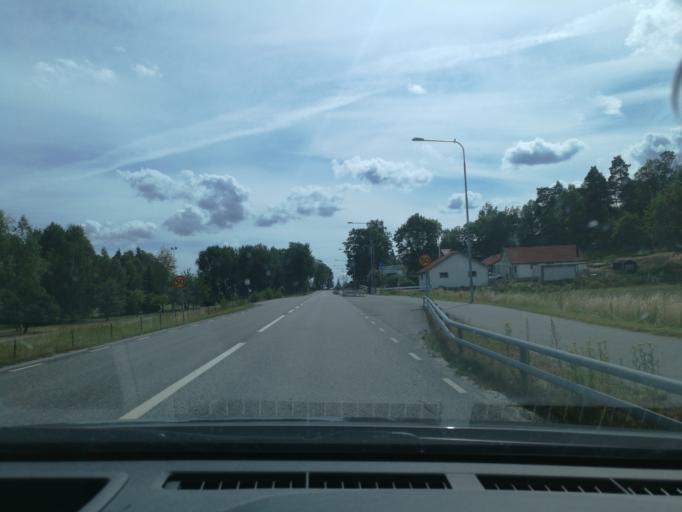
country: SE
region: Stockholm
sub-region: Sigtuna Kommun
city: Rosersberg
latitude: 59.6053
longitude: 17.8814
